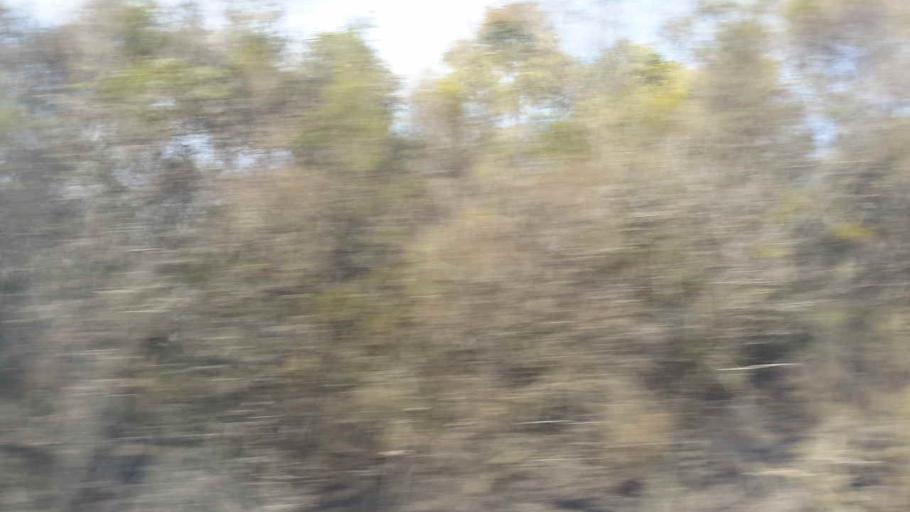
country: AU
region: New South Wales
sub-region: Wollongong
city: Bulli
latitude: -34.2450
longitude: 150.8449
